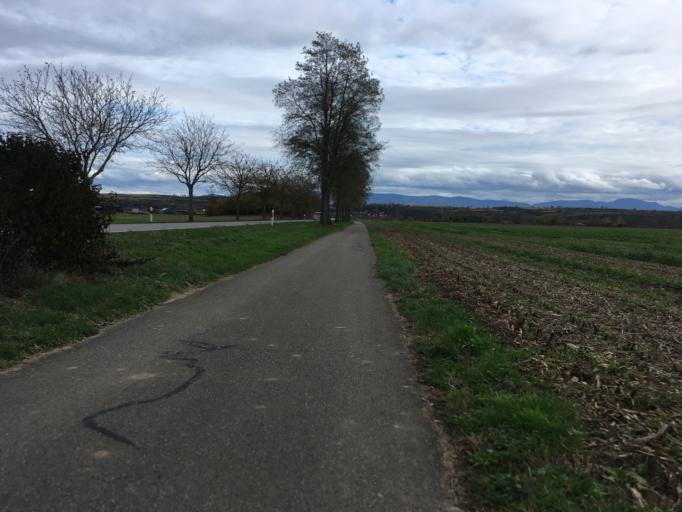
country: DE
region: Baden-Wuerttemberg
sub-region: Freiburg Region
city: Merdingen
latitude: 48.0261
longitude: 7.6669
